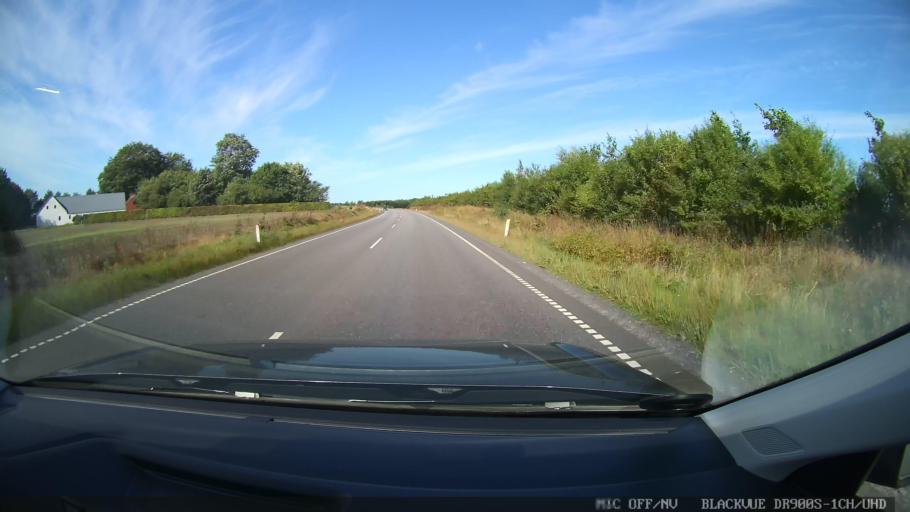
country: DK
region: North Denmark
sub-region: Mariagerfjord Kommune
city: Hobro
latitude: 56.6648
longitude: 9.7732
